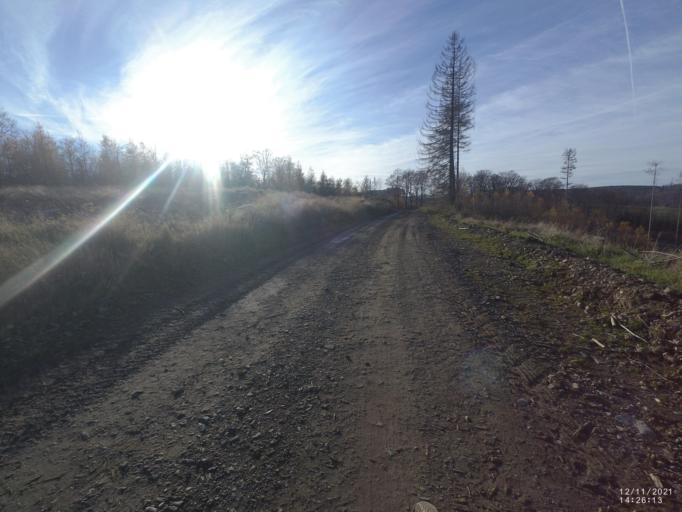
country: DE
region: North Rhine-Westphalia
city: Meinerzhagen
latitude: 51.1559
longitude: 7.6858
